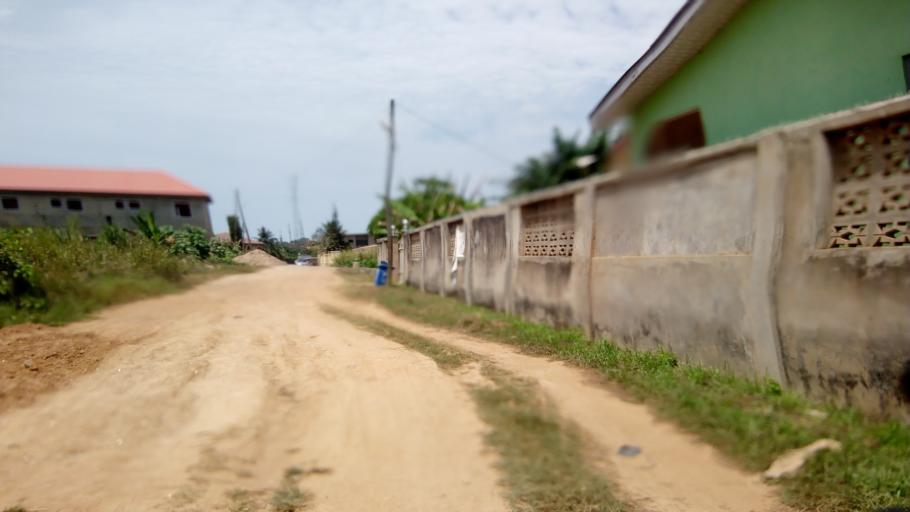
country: GH
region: Central
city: Cape Coast
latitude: 5.1239
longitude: -1.2747
